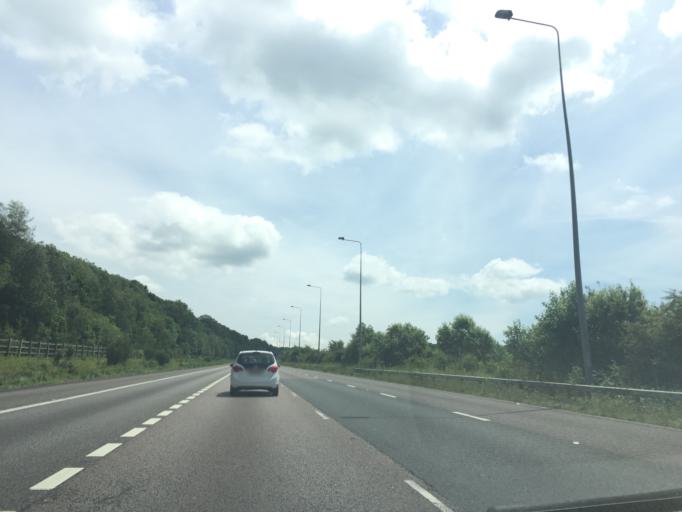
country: GB
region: England
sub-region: Medway
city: Rochester
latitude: 51.3496
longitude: 0.5003
